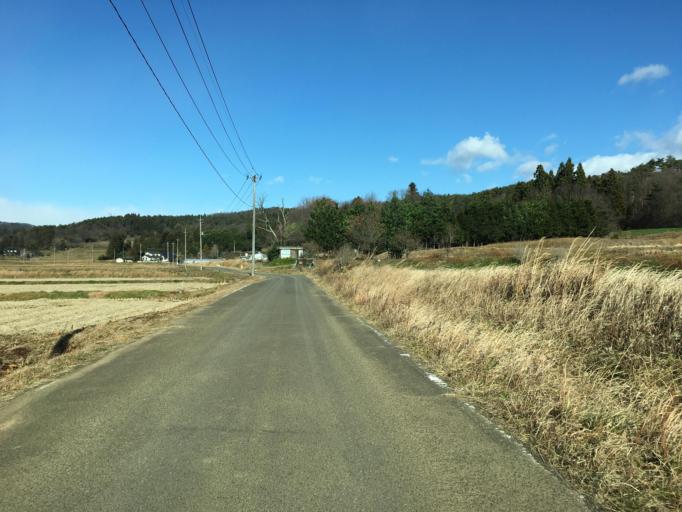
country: JP
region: Fukushima
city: Nihommatsu
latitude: 37.5795
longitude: 140.3960
